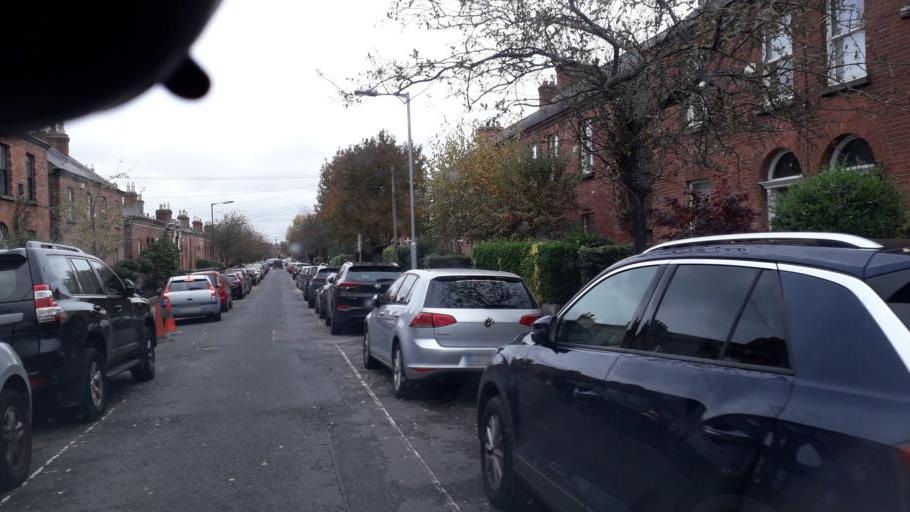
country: IE
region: Leinster
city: Rathmines
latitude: 53.3195
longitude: -6.2536
